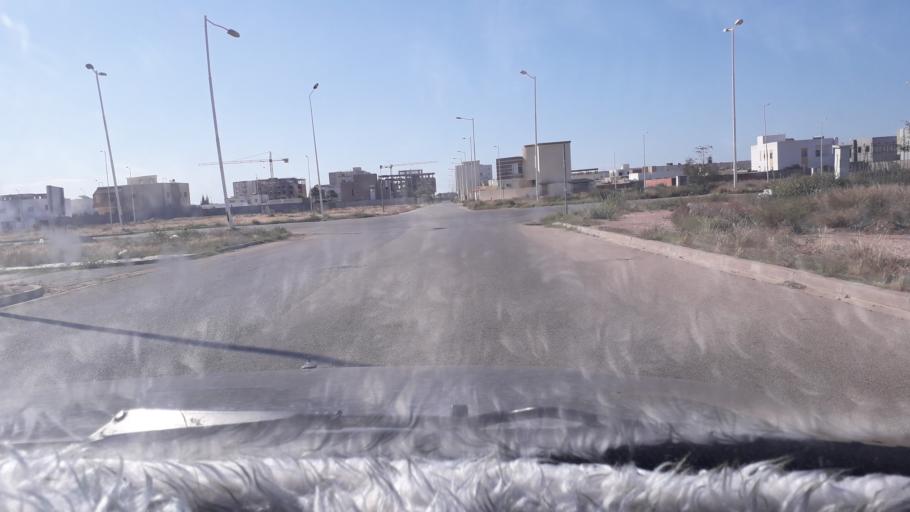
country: TN
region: Safaqis
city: Al Qarmadah
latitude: 34.8368
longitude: 10.7556
